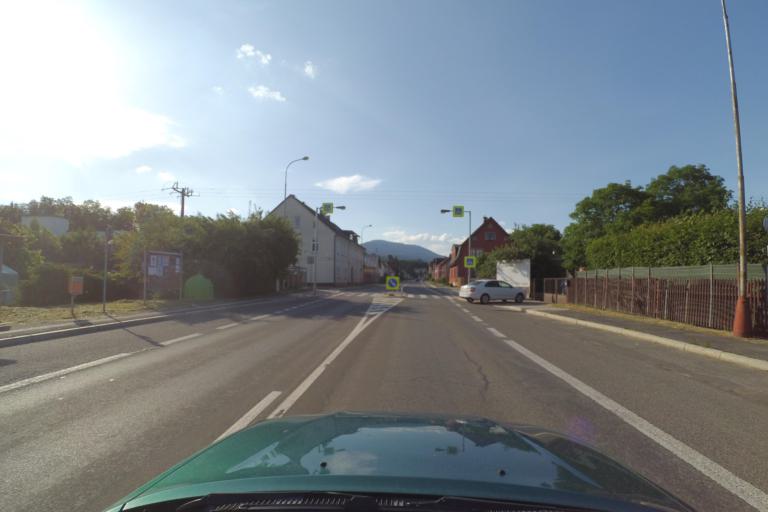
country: CZ
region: Kralovehradecky
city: Mlade Buky
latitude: 50.6135
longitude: 15.8228
